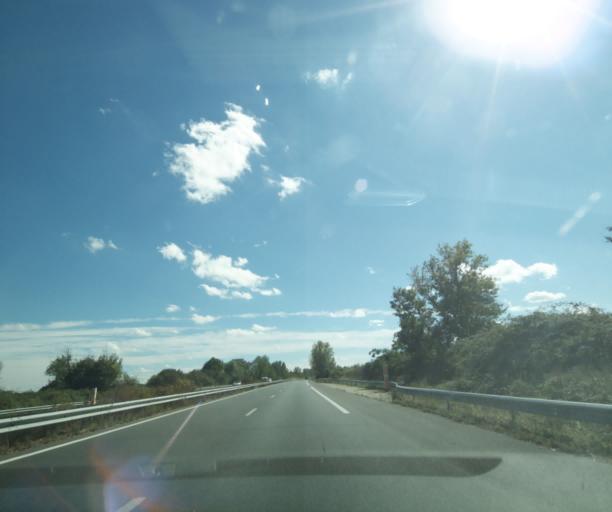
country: FR
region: Aquitaine
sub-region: Departement du Lot-et-Garonne
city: Tonneins
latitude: 44.3625
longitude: 0.2452
